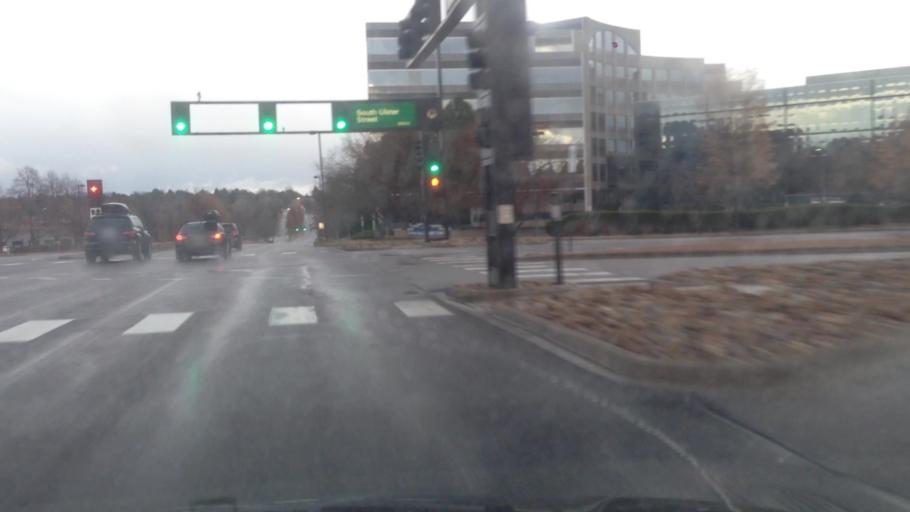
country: US
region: Colorado
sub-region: Arapahoe County
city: Castlewood
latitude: 39.6240
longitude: -104.8949
